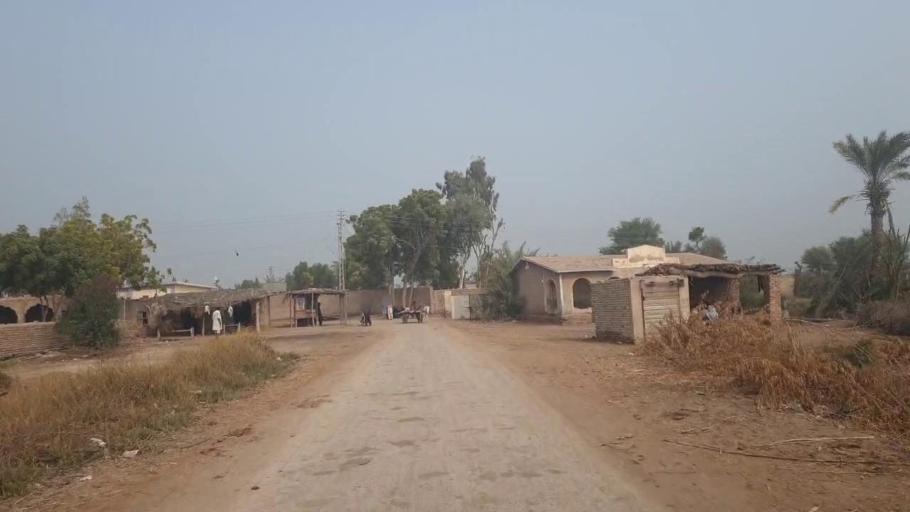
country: PK
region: Sindh
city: Bhit Shah
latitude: 25.8051
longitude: 68.5656
